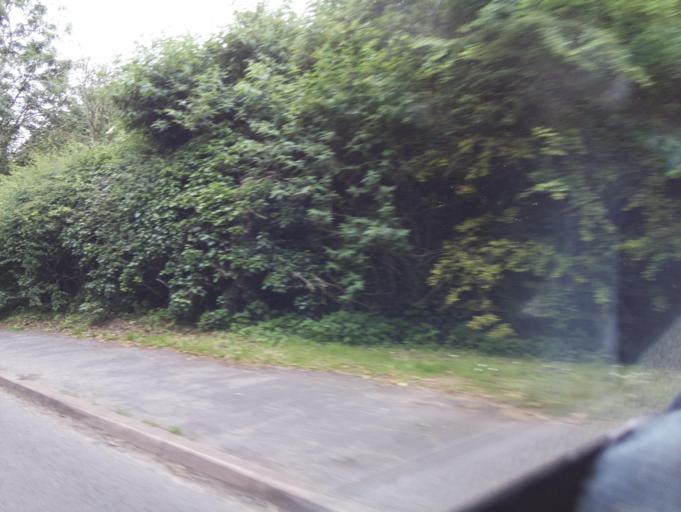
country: GB
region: England
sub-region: District of Rutland
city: Edith Weston
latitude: 52.6376
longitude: -0.6280
